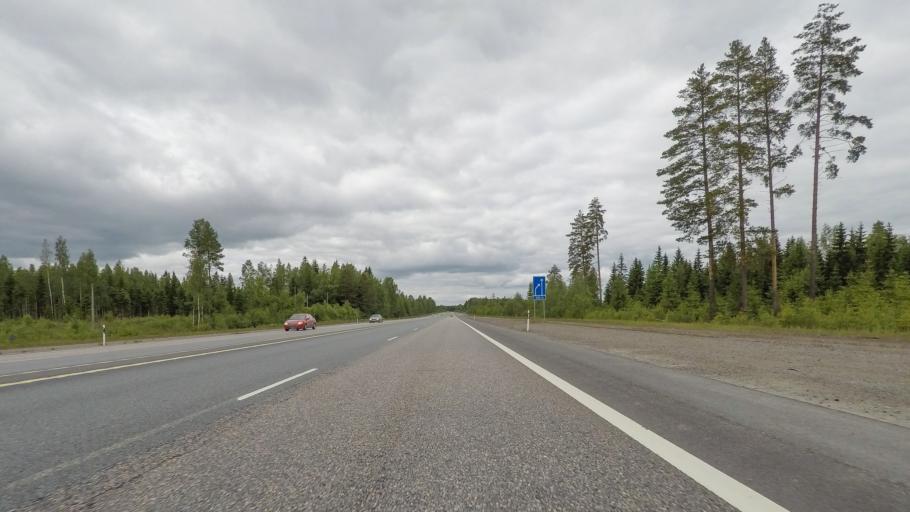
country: FI
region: Central Finland
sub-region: Joutsa
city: Joutsa
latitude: 61.7700
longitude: 26.1016
